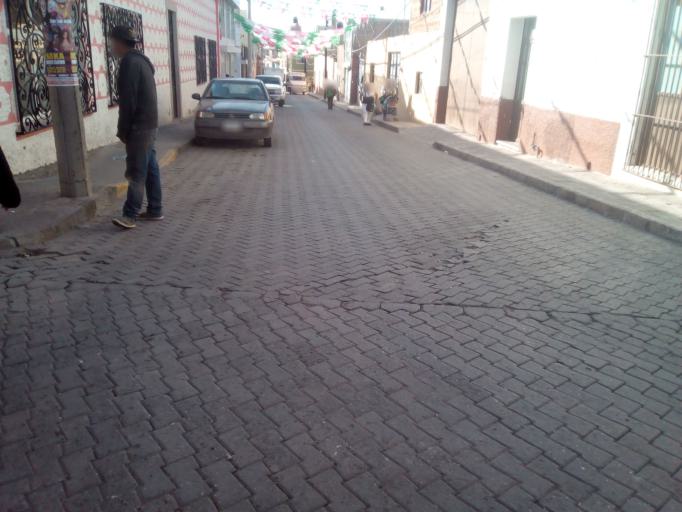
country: MX
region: Guanajuato
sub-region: San Luis de la Paz
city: San Luis de la Paz
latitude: 21.2973
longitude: -100.5126
